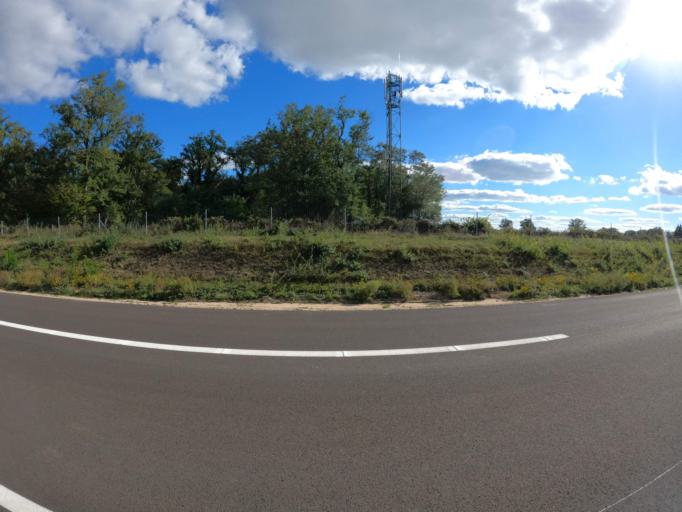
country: FR
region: Auvergne
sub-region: Departement de l'Allier
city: Lusigny
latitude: 46.5362
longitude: 3.5386
